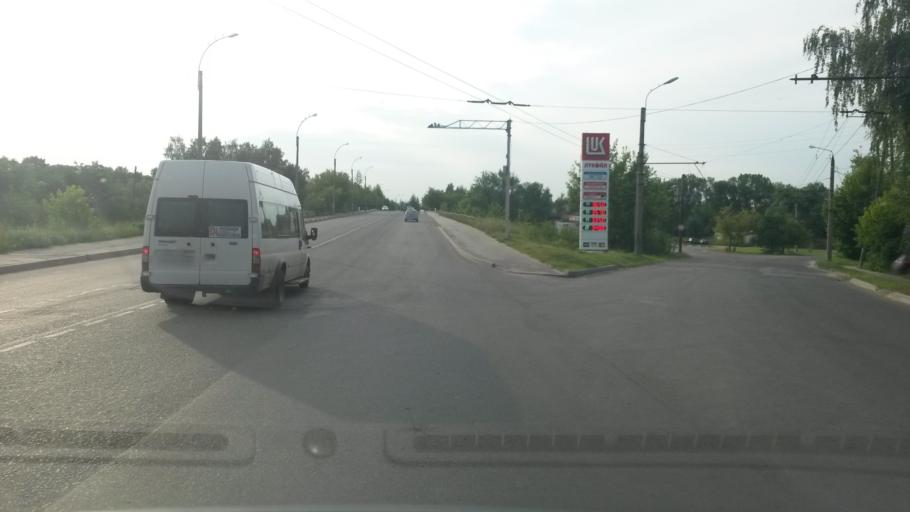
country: RU
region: Ivanovo
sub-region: Gorod Ivanovo
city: Ivanovo
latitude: 57.0161
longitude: 40.9285
